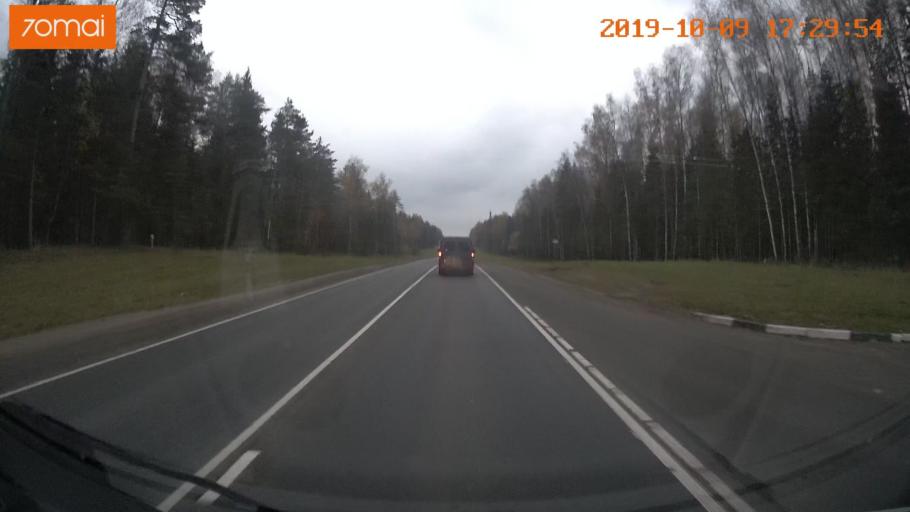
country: RU
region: Ivanovo
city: Bogorodskoye
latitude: 57.1466
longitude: 41.0547
